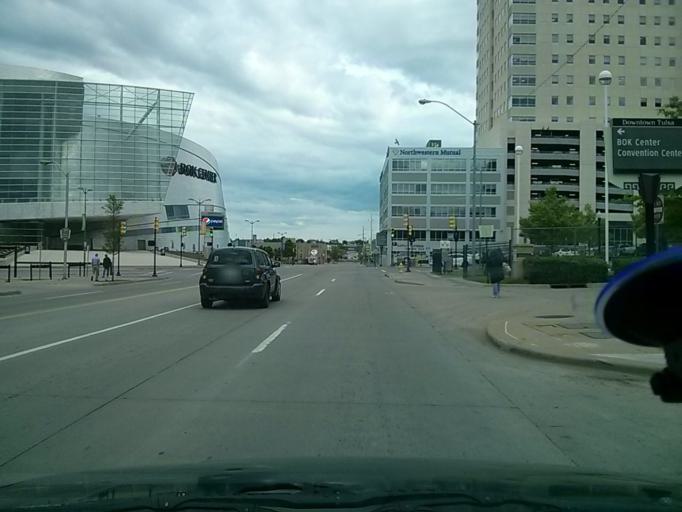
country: US
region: Oklahoma
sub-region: Tulsa County
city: Tulsa
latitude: 36.1517
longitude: -95.9943
